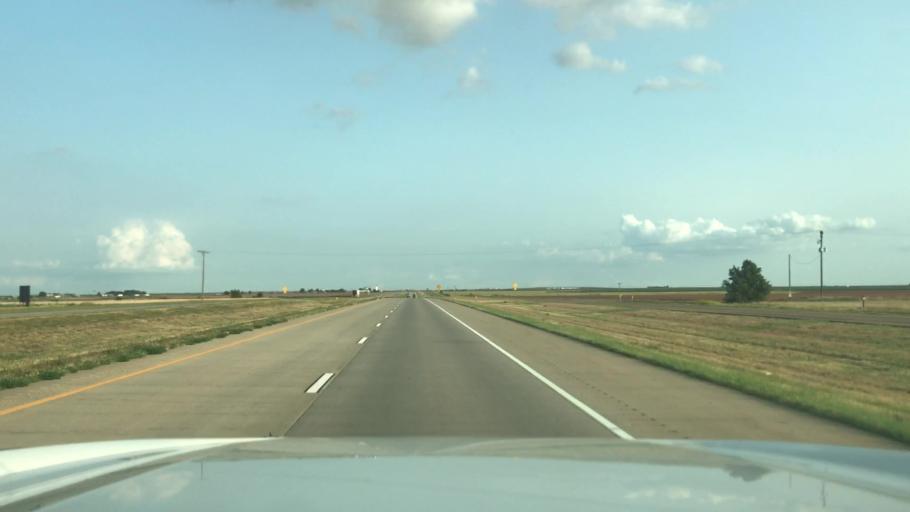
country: US
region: Texas
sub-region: Swisher County
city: Tulia
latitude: 34.5016
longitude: -101.7866
